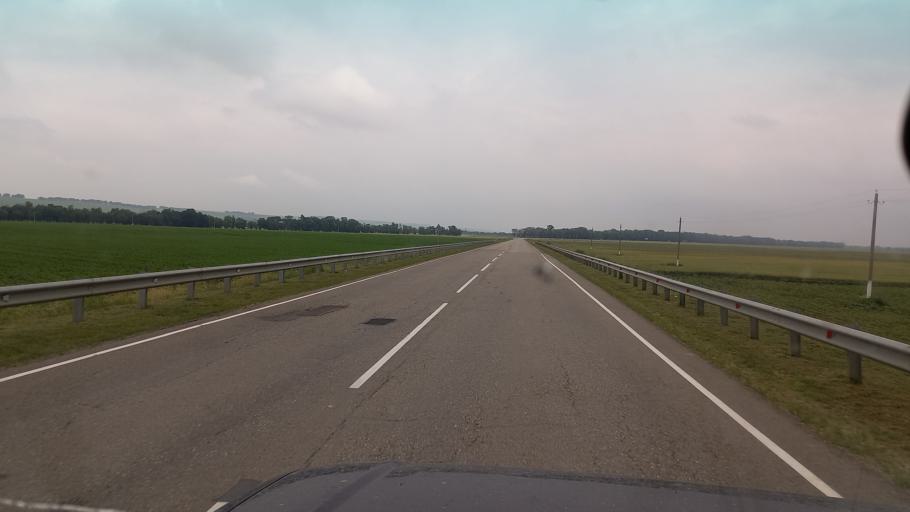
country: RU
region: Adygeya
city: Khodz'
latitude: 44.5359
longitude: 40.7180
